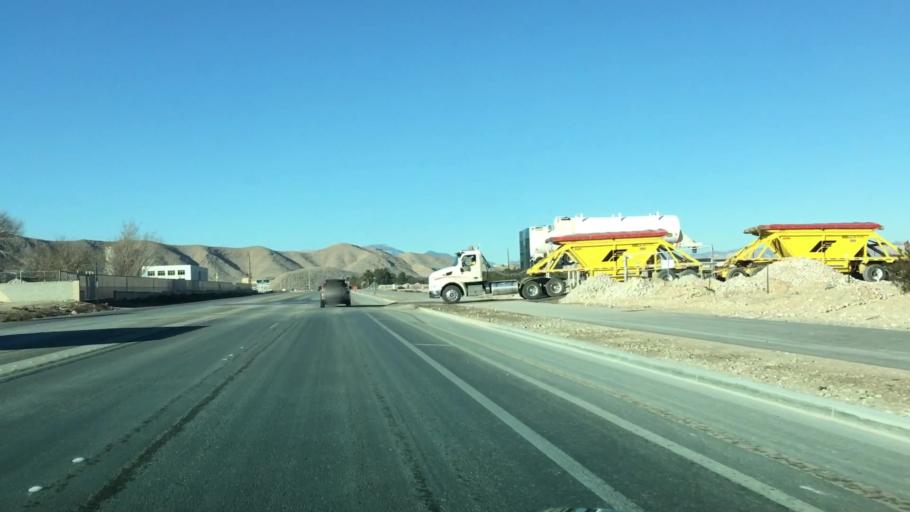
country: US
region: Nevada
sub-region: Clark County
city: Enterprise
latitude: 35.9629
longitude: -115.1606
